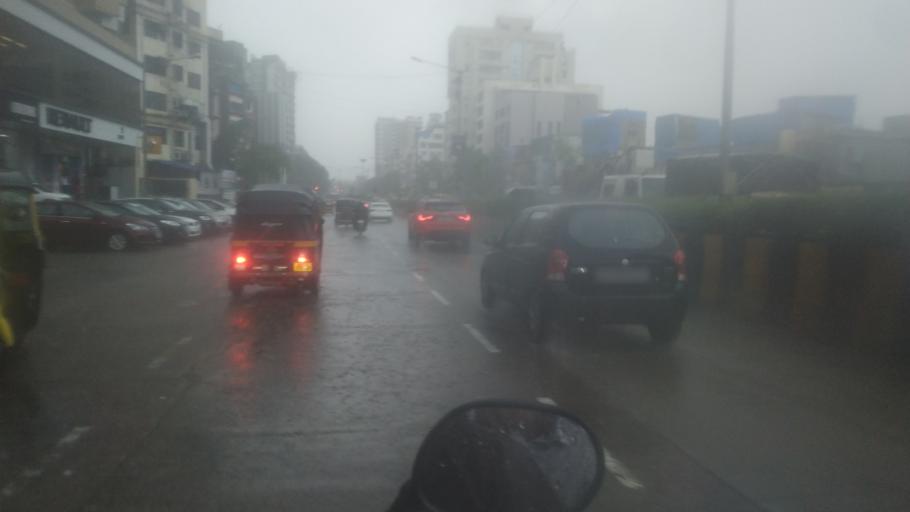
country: IN
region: Maharashtra
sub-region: Mumbai Suburban
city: Mumbai
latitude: 19.1159
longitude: 72.8361
